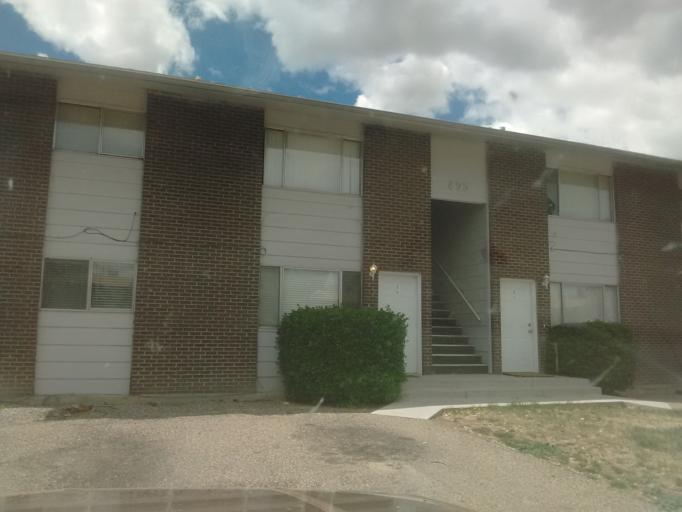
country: US
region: Colorado
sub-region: Mesa County
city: Clifton
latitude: 39.0761
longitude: -108.4567
